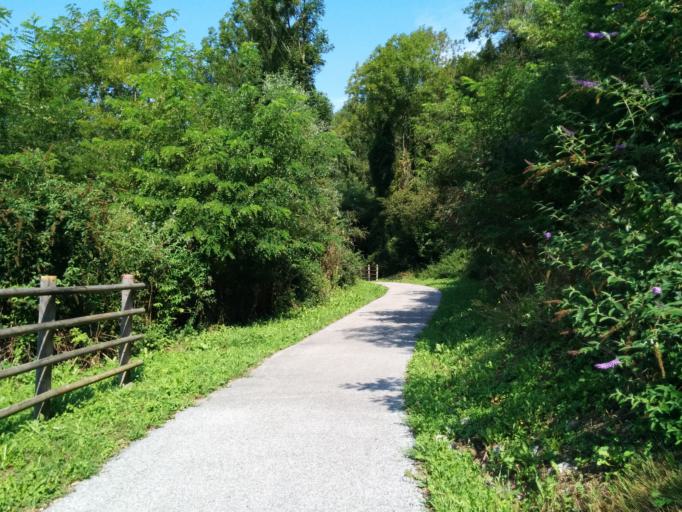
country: IT
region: Friuli Venezia Giulia
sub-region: Provincia di Udine
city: Villa Santina
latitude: 46.4261
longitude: 12.9042
